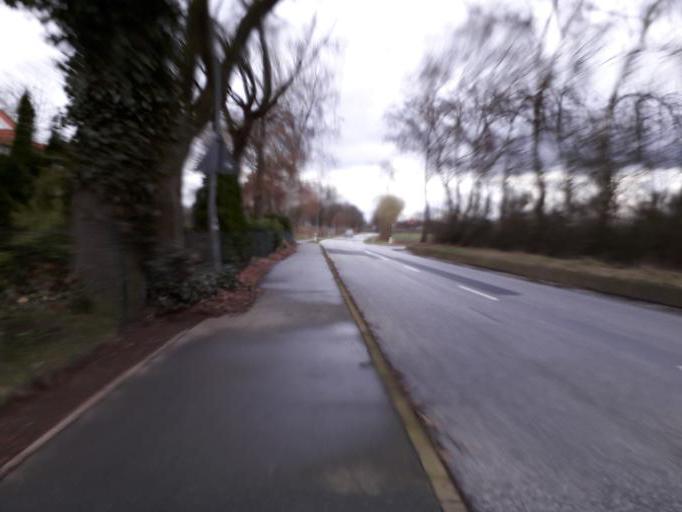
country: DE
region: Schleswig-Holstein
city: Glinde
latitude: 53.5611
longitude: 10.2099
